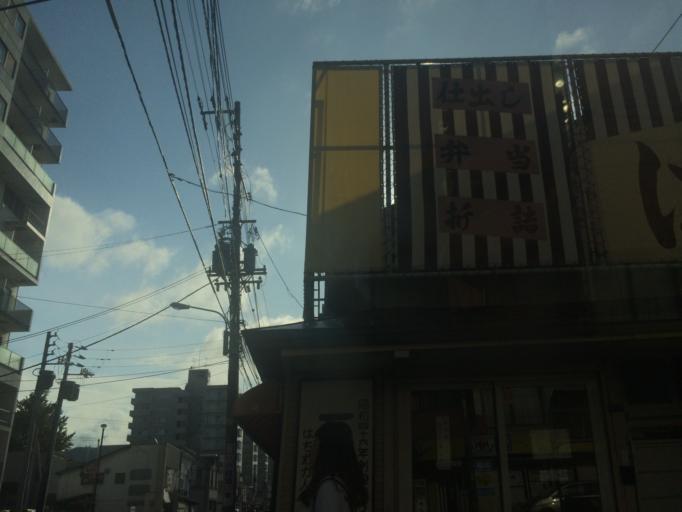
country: JP
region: Hokkaido
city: Sapporo
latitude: 43.0414
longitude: 141.3506
